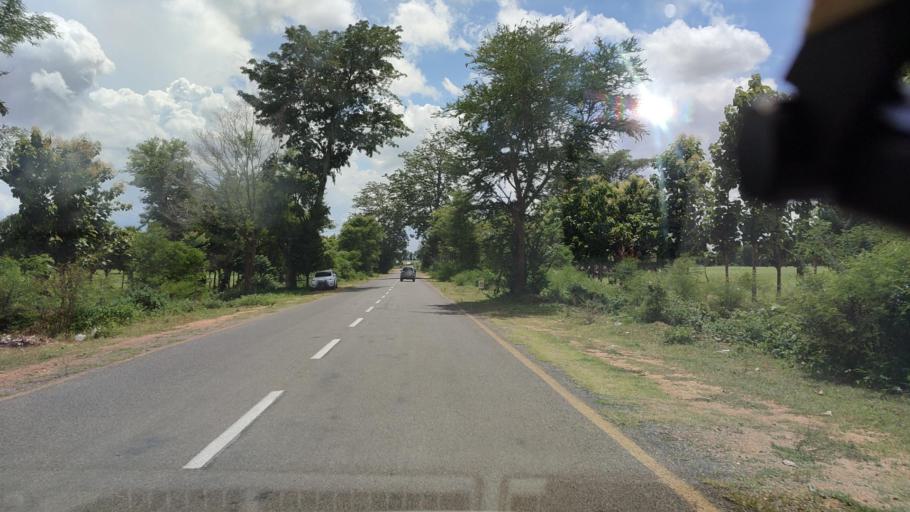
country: MM
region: Magway
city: Magway
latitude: 20.1900
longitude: 95.0501
